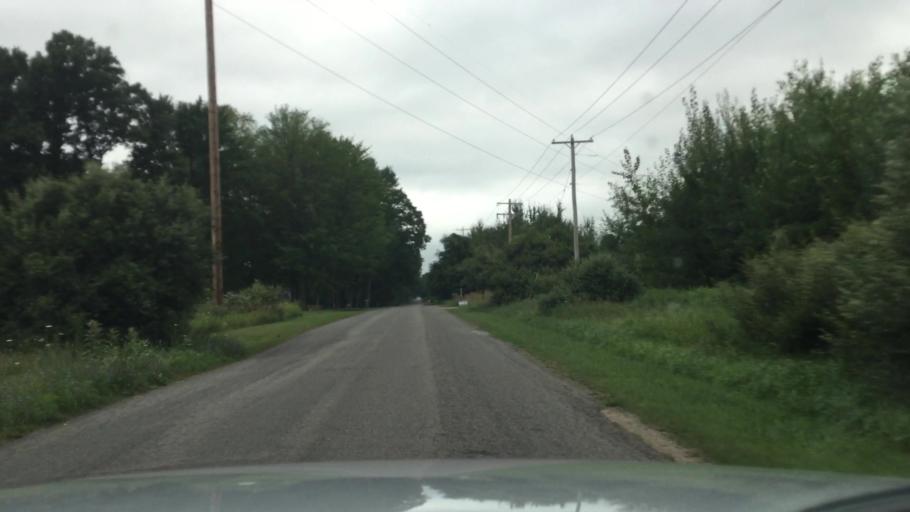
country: US
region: Michigan
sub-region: Montcalm County
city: Greenville
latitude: 43.1750
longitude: -85.2234
